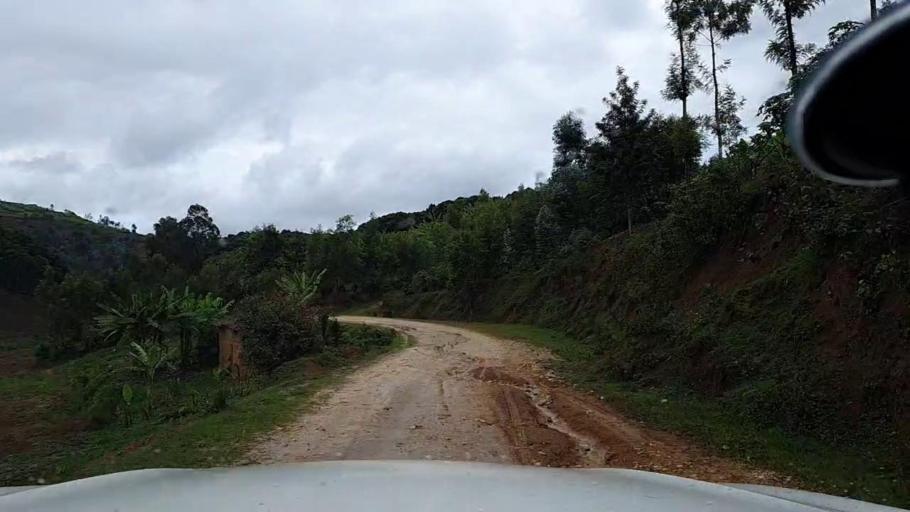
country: RW
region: Western Province
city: Kibuye
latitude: -2.1158
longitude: 29.4920
